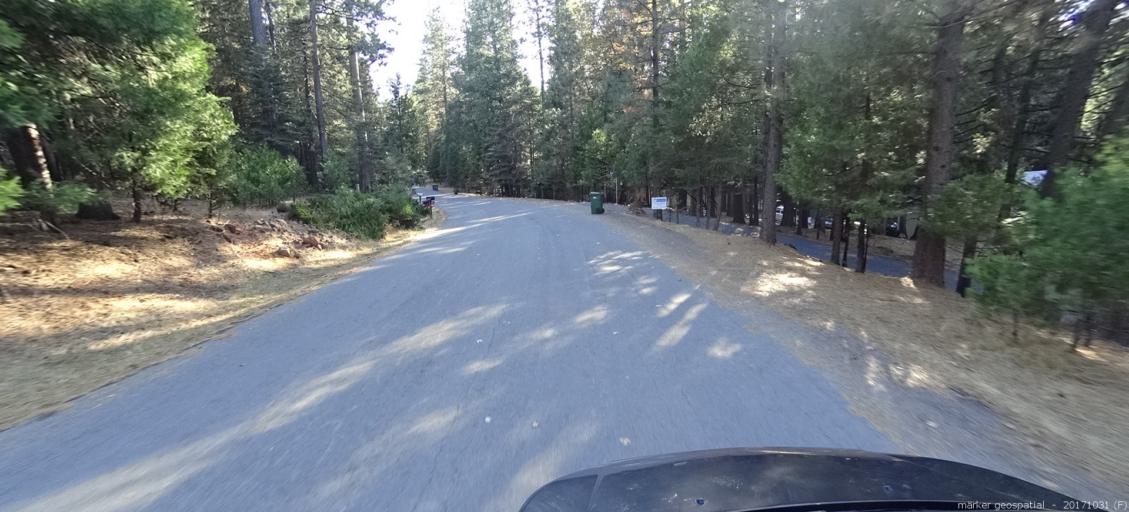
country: US
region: California
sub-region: Shasta County
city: Shingletown
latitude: 40.4989
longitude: -121.9039
